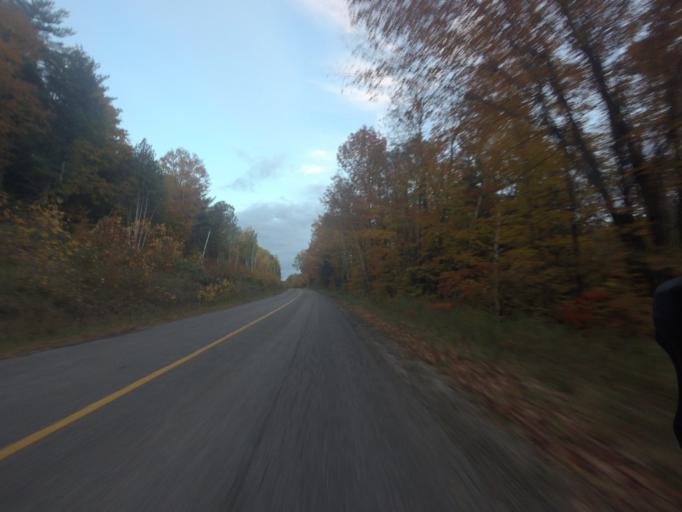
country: CA
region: Ontario
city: Renfrew
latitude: 45.3564
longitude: -76.9594
